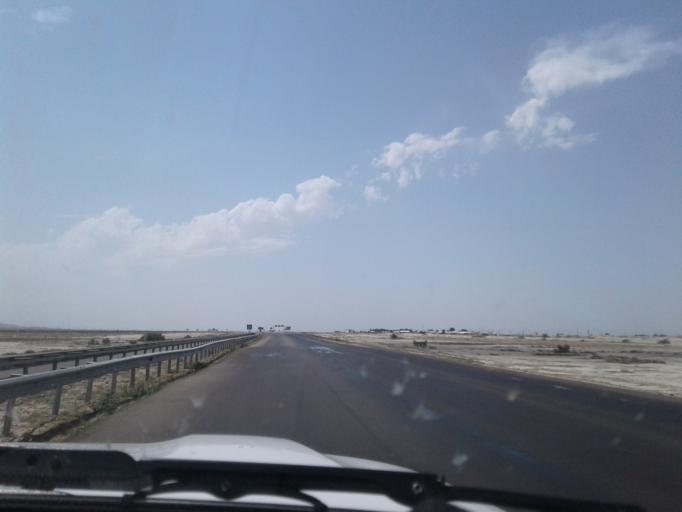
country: IR
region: Razavi Khorasan
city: Dargaz
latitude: 37.7140
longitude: 59.0206
